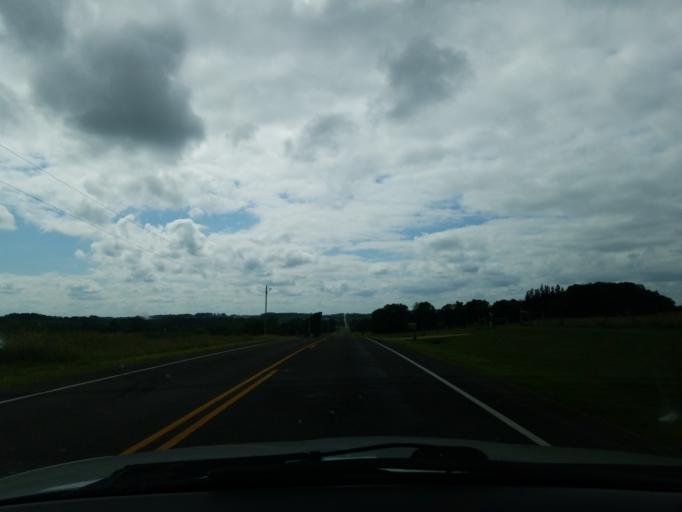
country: US
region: Wisconsin
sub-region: Saint Croix County
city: Glenwood City
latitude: 44.9882
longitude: -92.1769
